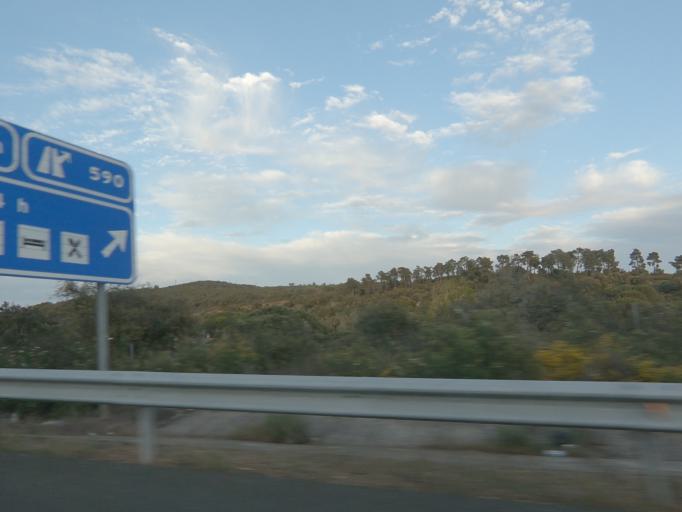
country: ES
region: Extremadura
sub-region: Provincia de Caceres
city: Alcuescar
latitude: 39.1546
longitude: -6.2738
